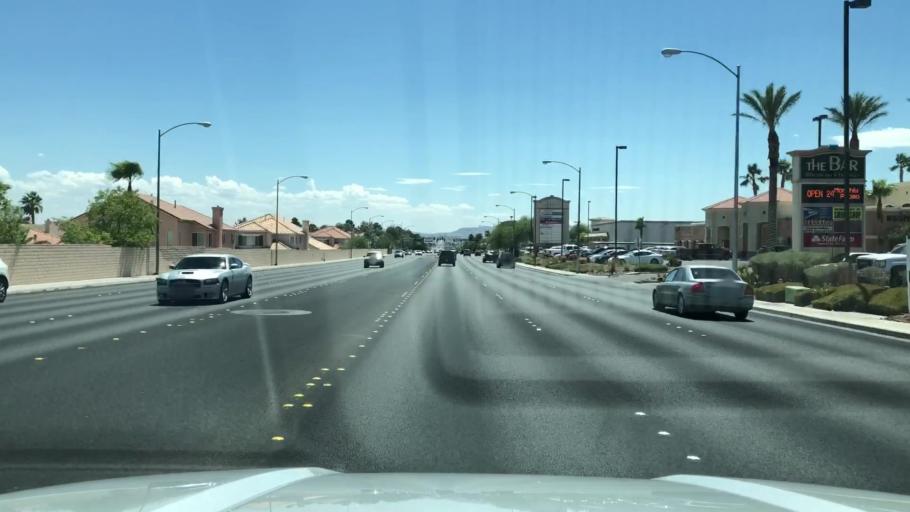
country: US
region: Nevada
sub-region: Clark County
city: Spring Valley
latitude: 36.1033
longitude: -115.2793
